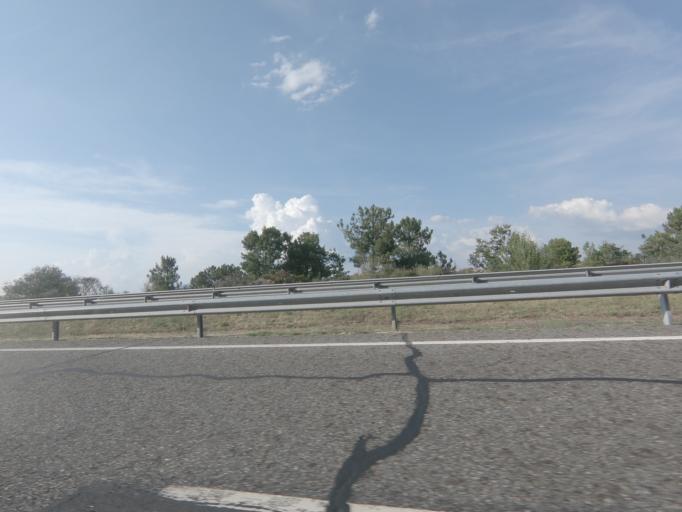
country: ES
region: Galicia
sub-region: Provincia de Ourense
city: Oimbra
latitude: 41.9247
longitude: -7.4845
